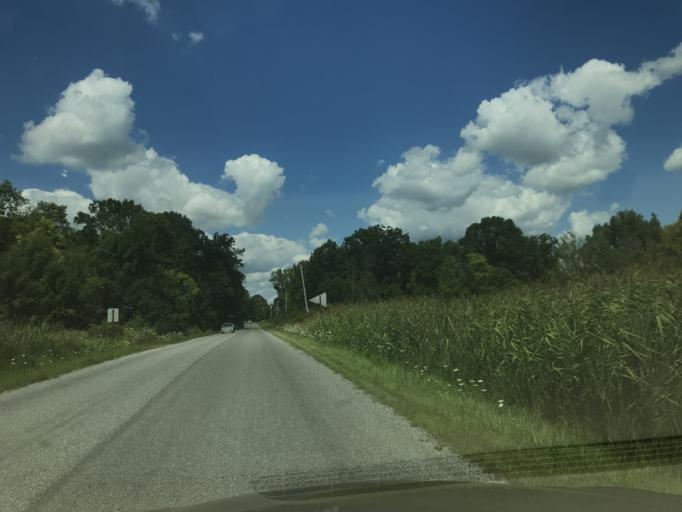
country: US
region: Michigan
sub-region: Ingham County
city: Holt
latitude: 42.6178
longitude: -84.5626
